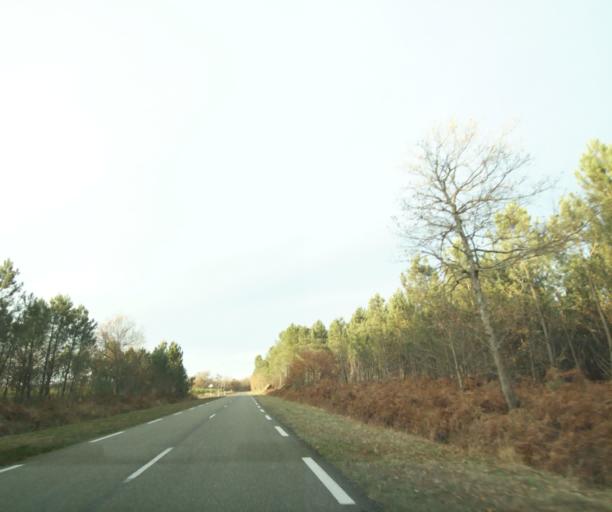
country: FR
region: Aquitaine
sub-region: Departement de la Gironde
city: Grignols
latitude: 44.1887
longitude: -0.1517
